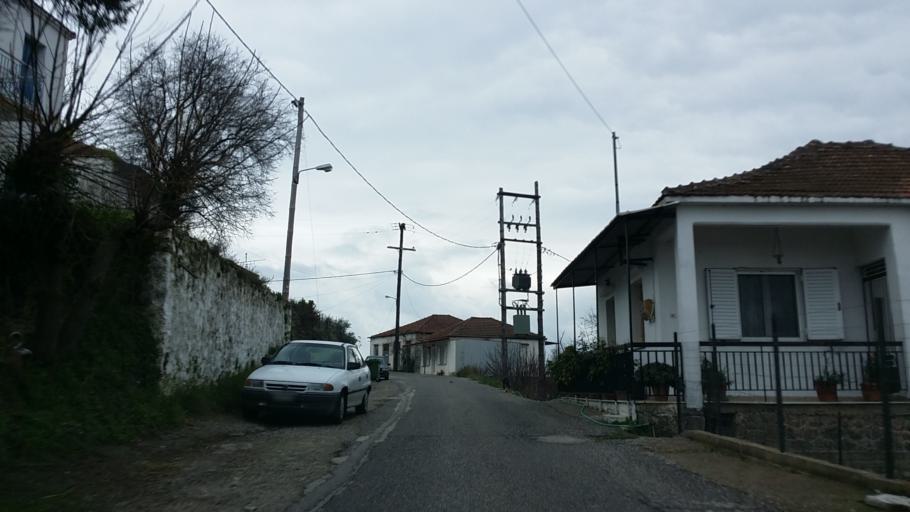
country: GR
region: West Greece
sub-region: Nomos Aitolias kai Akarnanias
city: Fitiai
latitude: 38.7093
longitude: 21.1699
